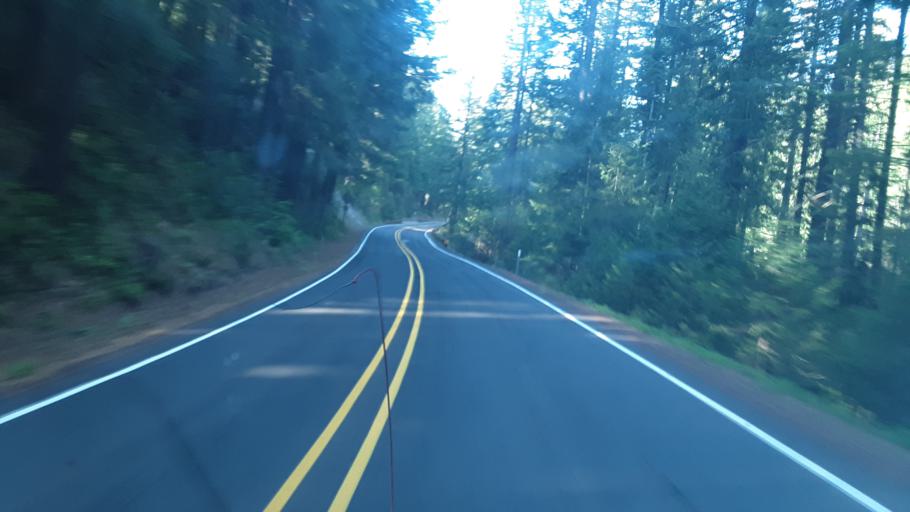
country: US
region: Oregon
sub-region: Jackson County
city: Shady Cove
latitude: 42.9349
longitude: -122.4216
